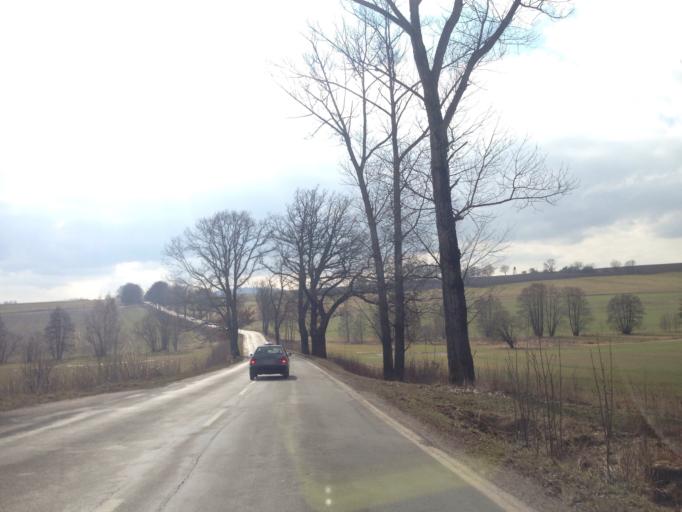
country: CZ
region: Kralovehradecky
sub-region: Okres Trutnov
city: Vrchlabi
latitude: 50.6032
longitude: 15.6000
